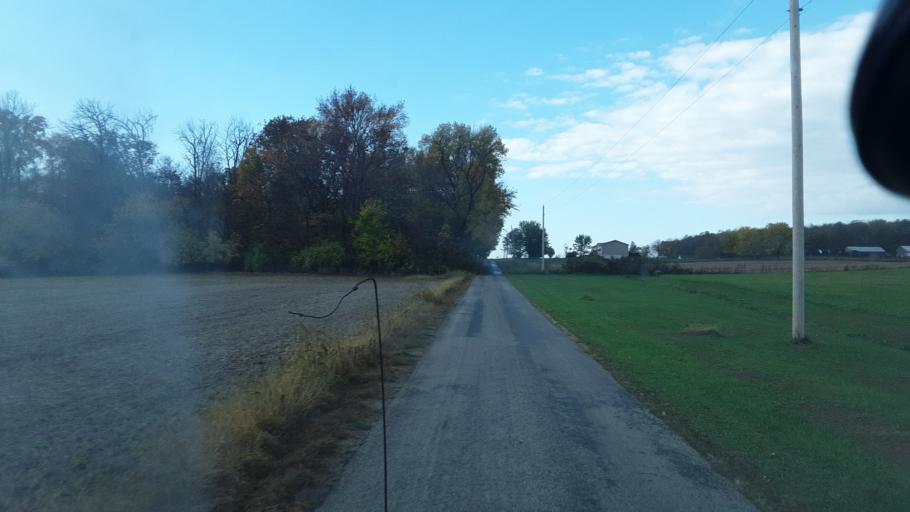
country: US
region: Ohio
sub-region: Highland County
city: Leesburg
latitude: 39.3226
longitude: -83.4779
